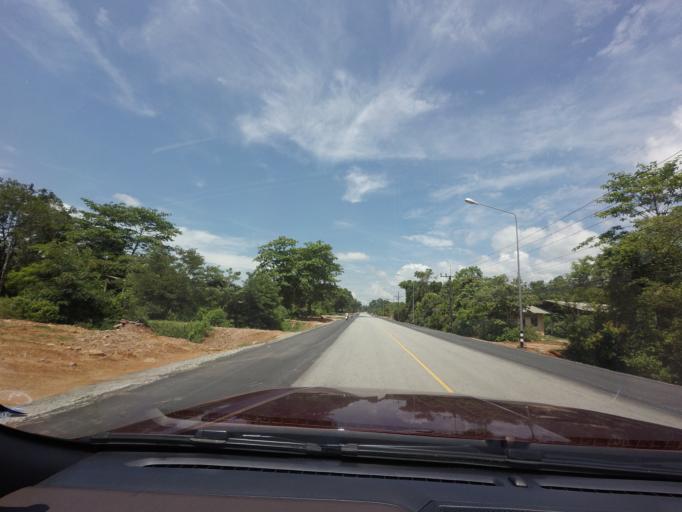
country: TH
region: Narathiwat
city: Ra-ngae
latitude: 6.2821
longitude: 101.7007
